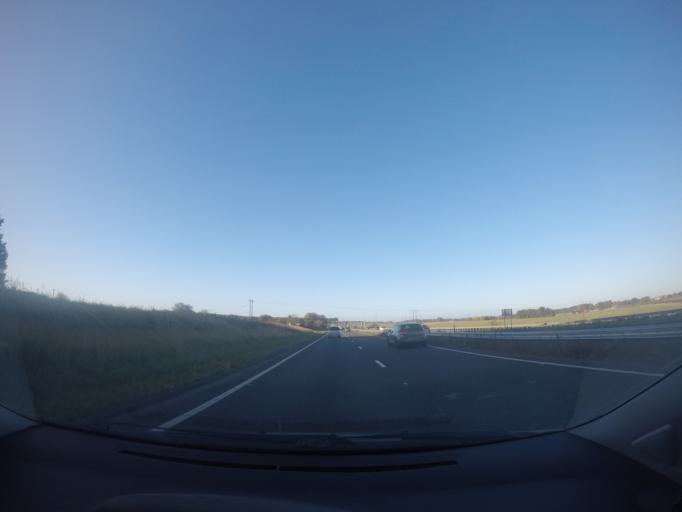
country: GB
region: England
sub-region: City and Borough of Leeds
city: Clifford
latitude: 53.8647
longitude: -1.3109
